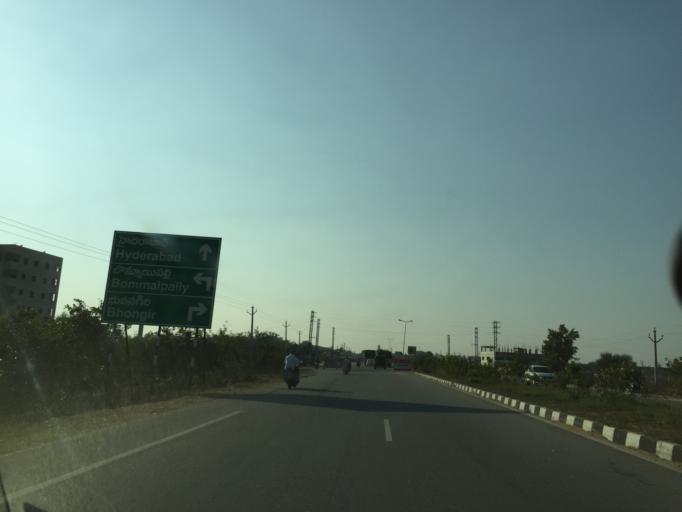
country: IN
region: Telangana
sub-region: Nalgonda
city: Bhongir
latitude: 17.5028
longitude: 78.8754
